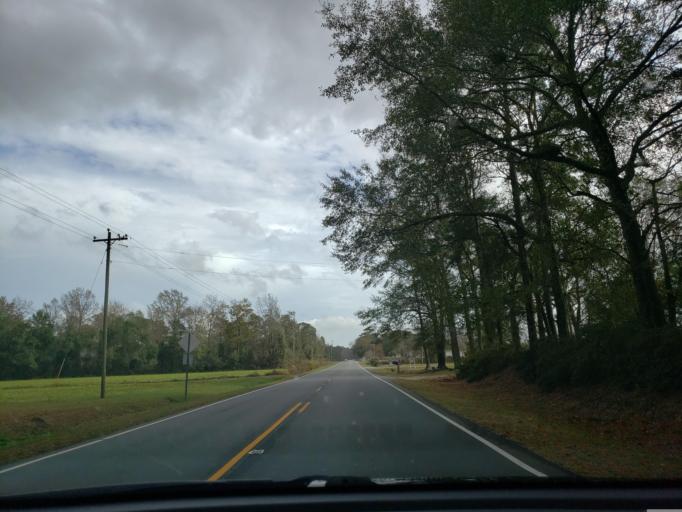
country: US
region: North Carolina
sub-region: Duplin County
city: Beulaville
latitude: 34.8378
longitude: -77.8609
